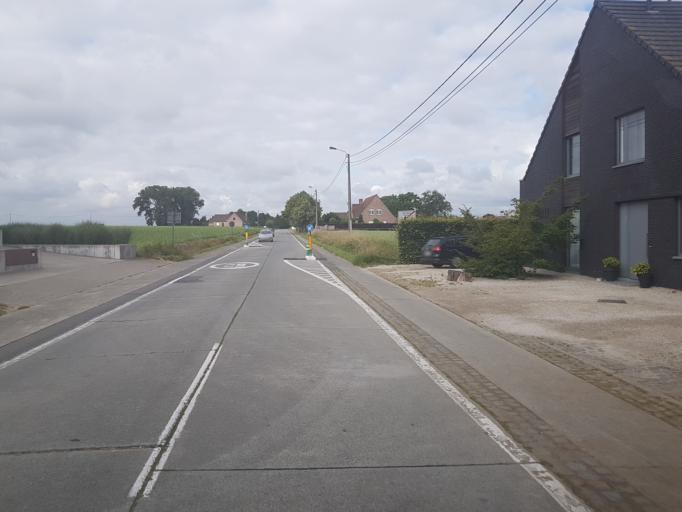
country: BE
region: Flanders
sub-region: Provincie West-Vlaanderen
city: Anzegem
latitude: 50.8471
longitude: 3.4384
